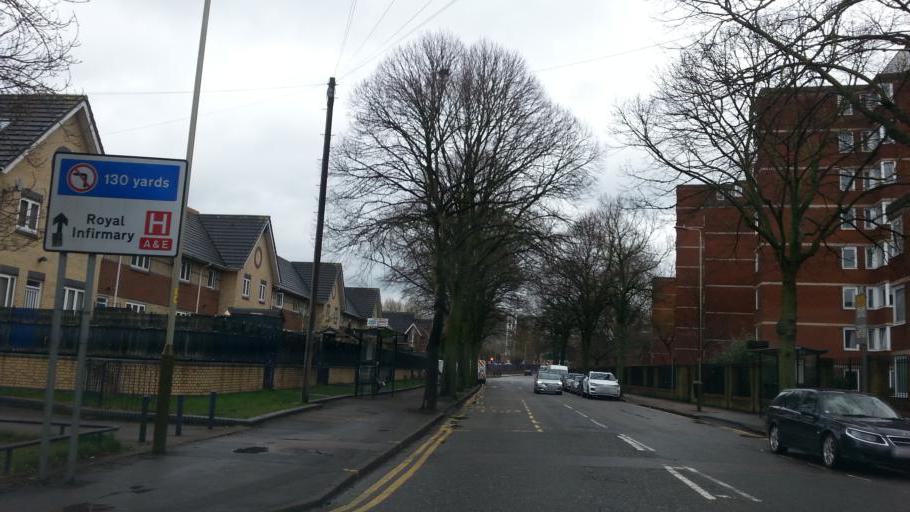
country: GB
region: England
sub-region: City of Leicester
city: Leicester
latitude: 52.6249
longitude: -1.1388
